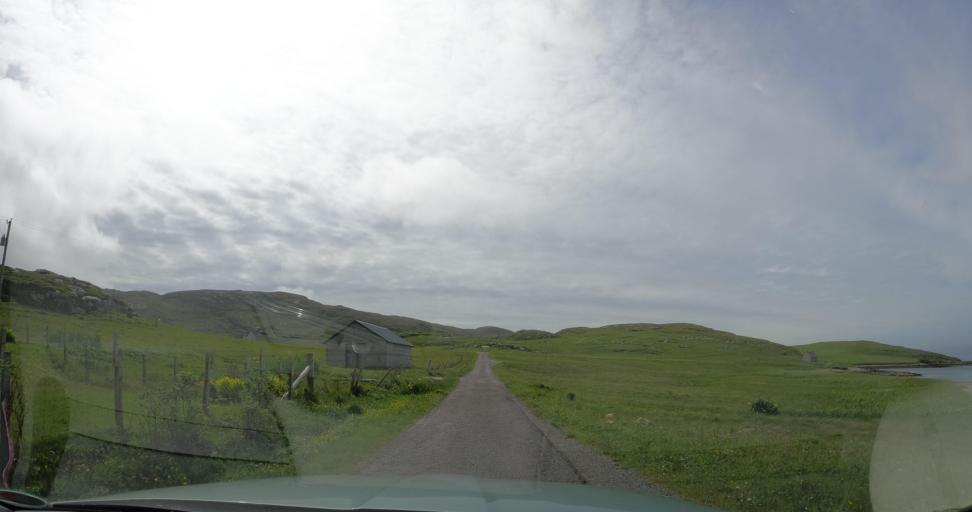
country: GB
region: Scotland
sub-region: Eilean Siar
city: Barra
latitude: 56.9443
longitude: -7.5411
